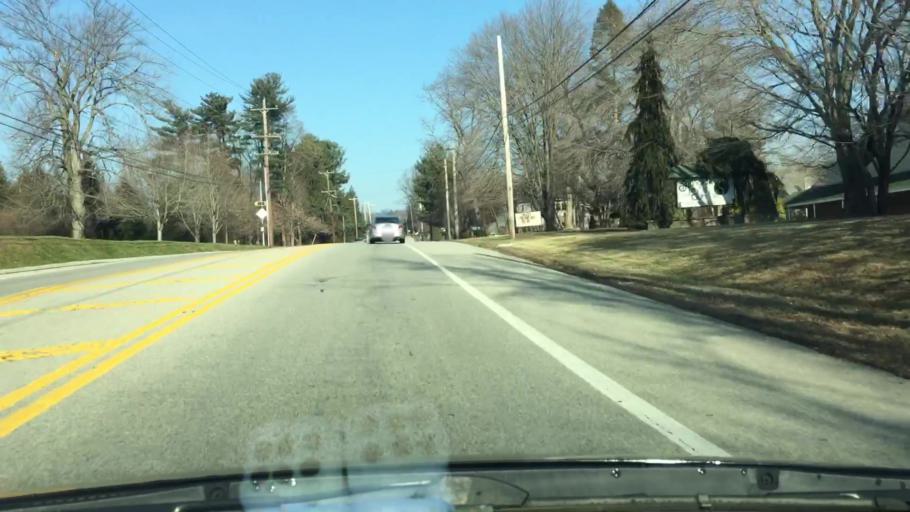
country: US
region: Pennsylvania
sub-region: Delaware County
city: Media
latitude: 39.9573
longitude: -75.3932
